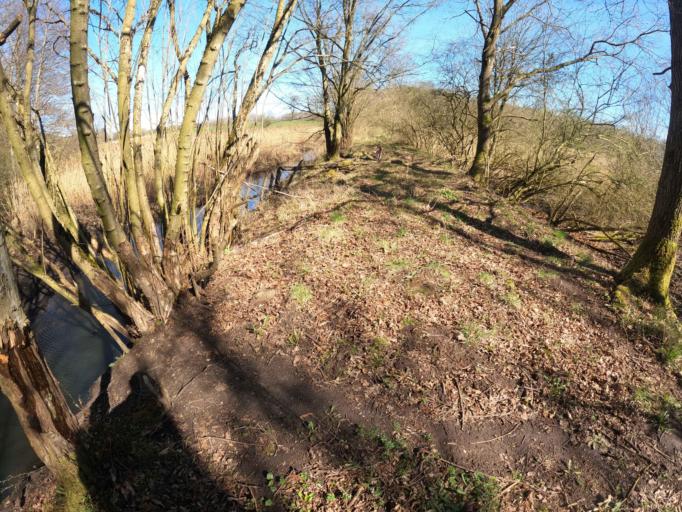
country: PL
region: West Pomeranian Voivodeship
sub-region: Powiat gryficki
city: Gryfice
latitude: 53.9301
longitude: 15.2771
